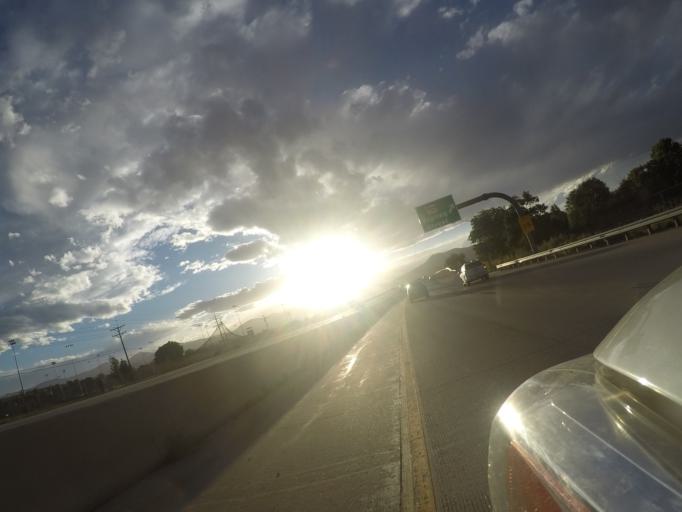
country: US
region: Colorado
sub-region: Jefferson County
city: Lakewood
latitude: 39.6535
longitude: -105.1054
